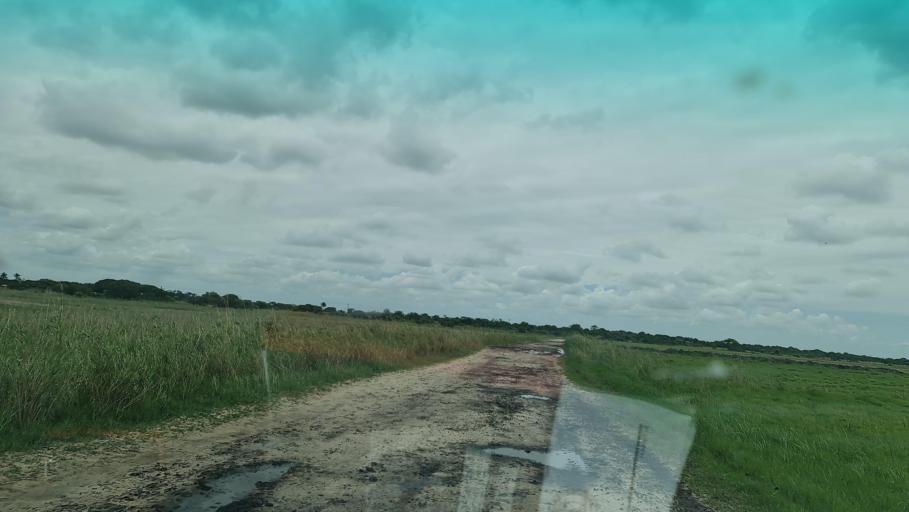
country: MZ
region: Maputo City
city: Maputo
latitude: -25.7054
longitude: 32.7037
